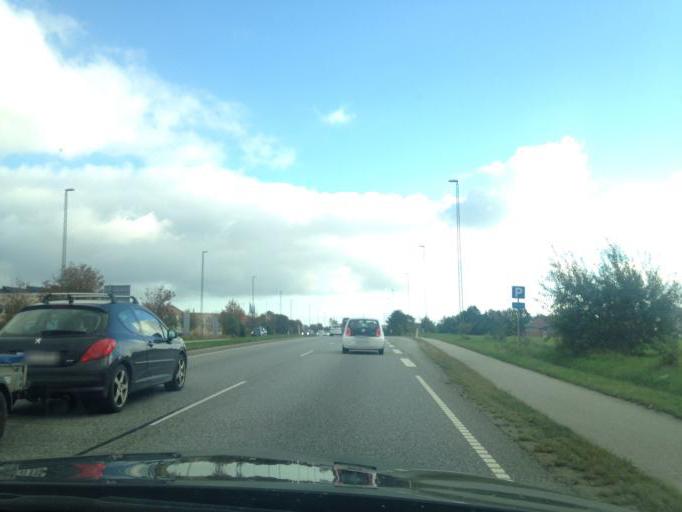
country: DK
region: South Denmark
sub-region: Vejle Kommune
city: Vejle
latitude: 55.6782
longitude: 9.5746
